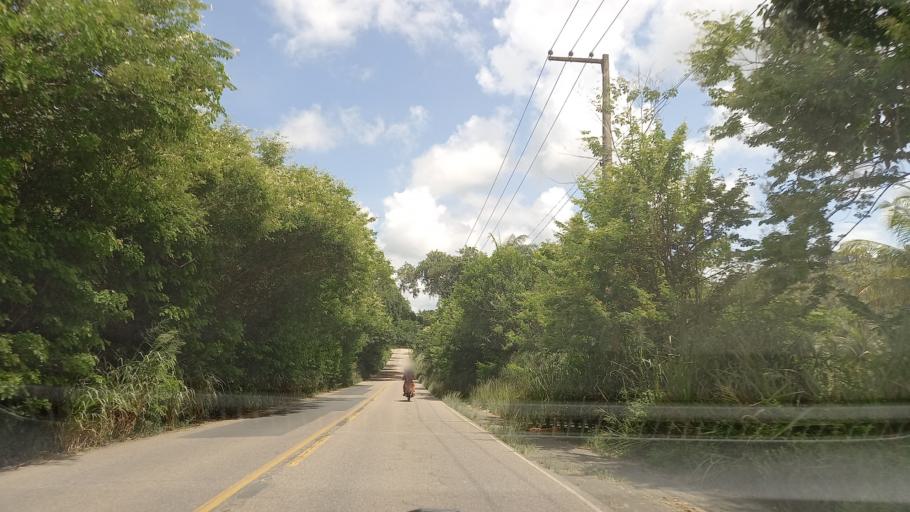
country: BR
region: Pernambuco
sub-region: Rio Formoso
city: Rio Formoso
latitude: -8.6531
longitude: -35.1345
